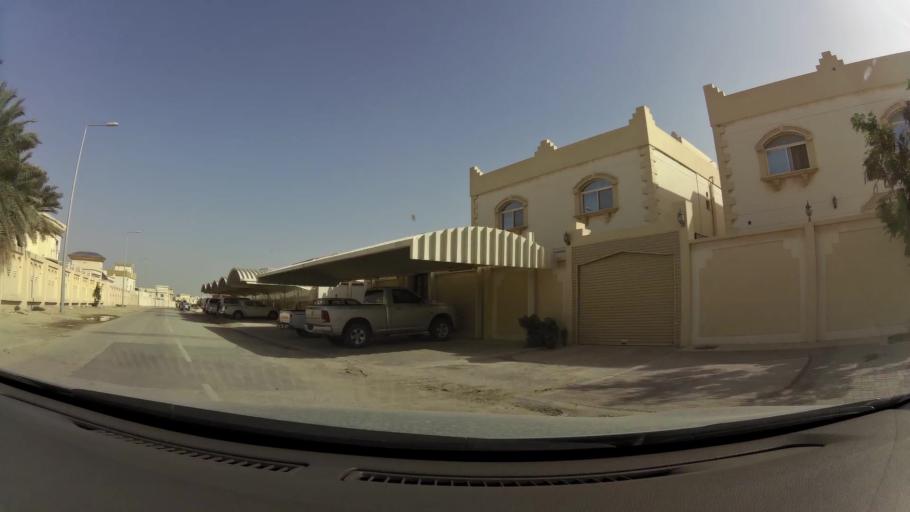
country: QA
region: Baladiyat ar Rayyan
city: Ar Rayyan
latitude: 25.3363
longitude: 51.4258
